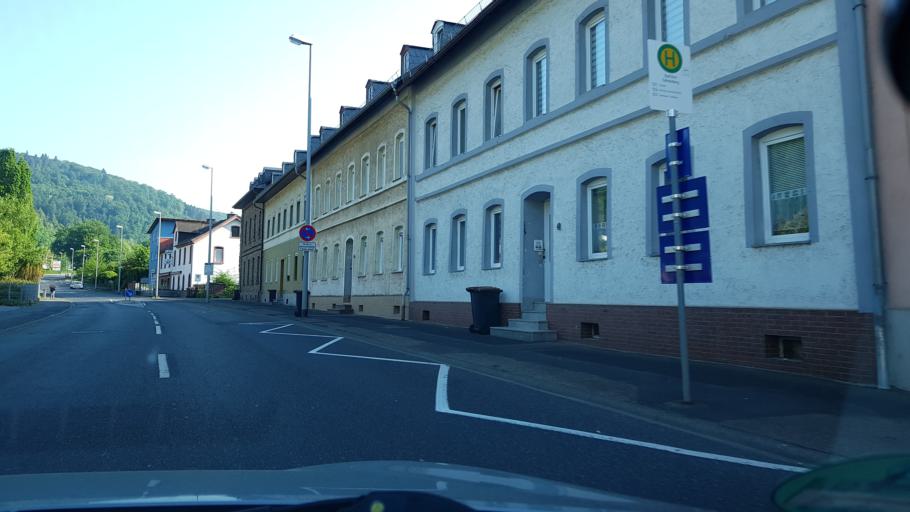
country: DE
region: Rheinland-Pfalz
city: Bad Ems
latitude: 50.3451
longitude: 7.7202
